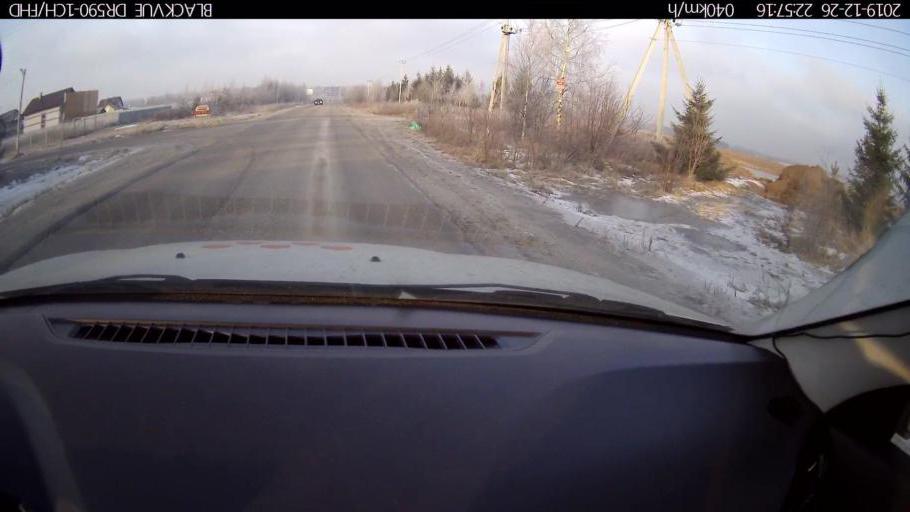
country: RU
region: Nizjnij Novgorod
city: Burevestnik
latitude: 56.1497
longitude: 43.7168
